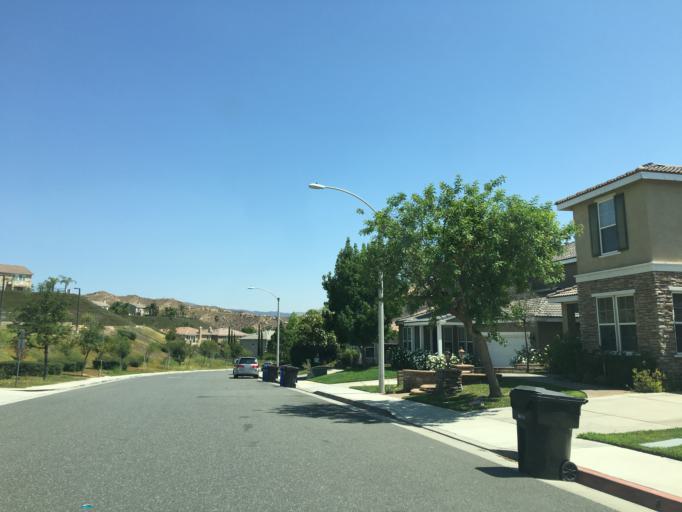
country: US
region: California
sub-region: Los Angeles County
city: Valencia
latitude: 34.4688
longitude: -118.5574
